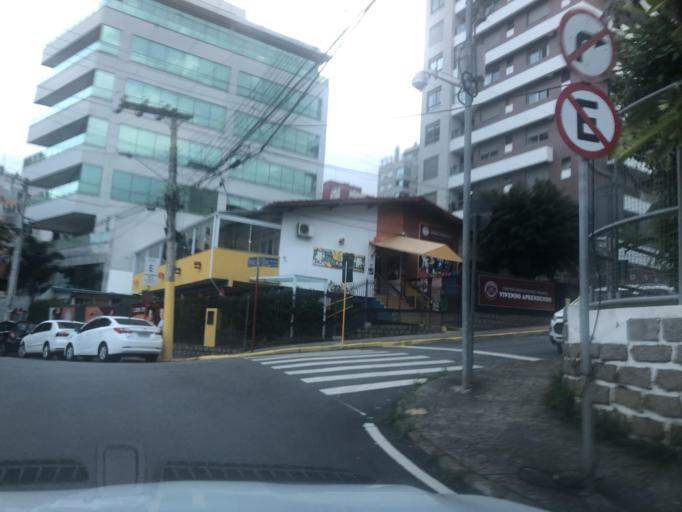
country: BR
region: Santa Catarina
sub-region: Florianopolis
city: Florianopolis
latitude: -27.5906
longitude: -48.5547
